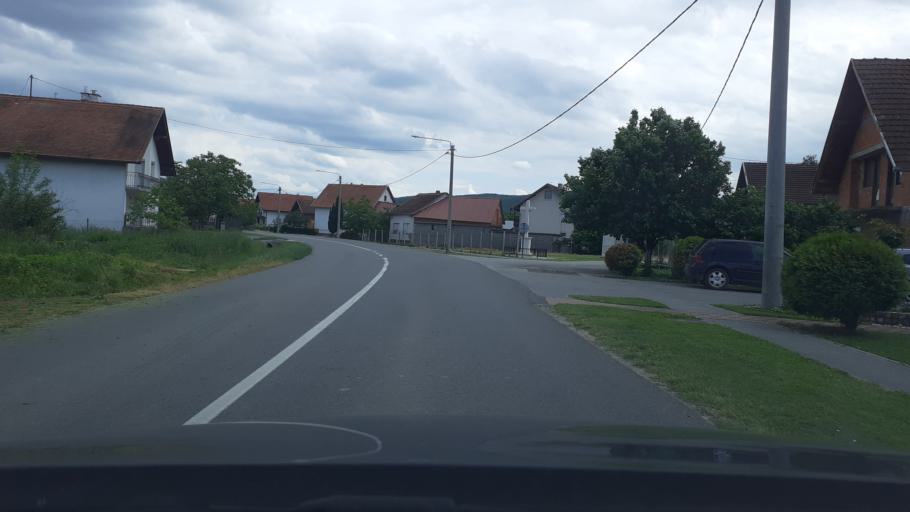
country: HR
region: Pozesko-Slavonska
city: Jaksic
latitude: 45.3409
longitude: 17.7563
